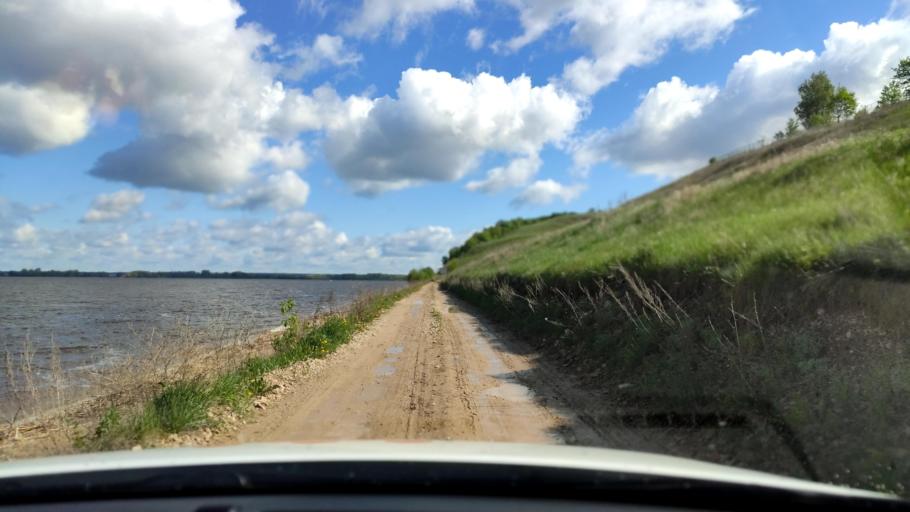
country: RU
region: Tatarstan
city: Sviyazhsk
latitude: 55.7737
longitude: 48.6889
